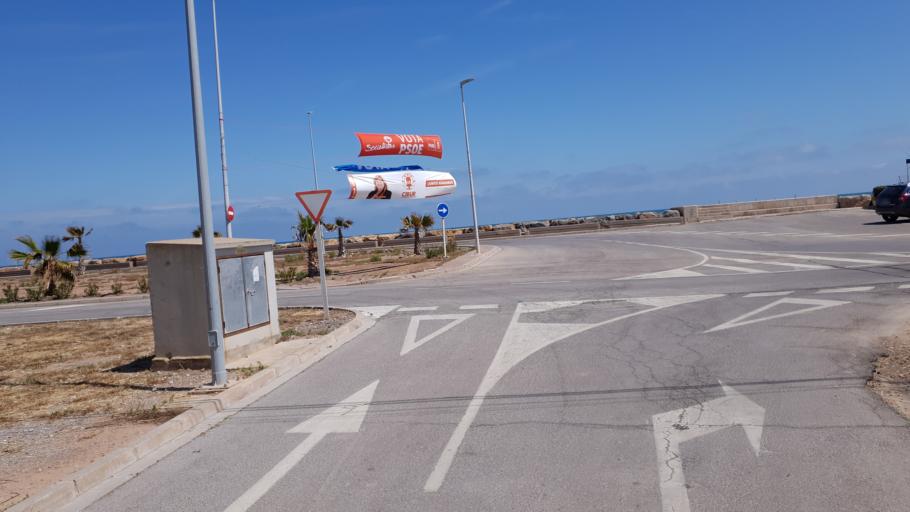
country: ES
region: Valencia
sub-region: Provincia de Castello
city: Burriana
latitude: 39.8577
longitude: -0.0861
